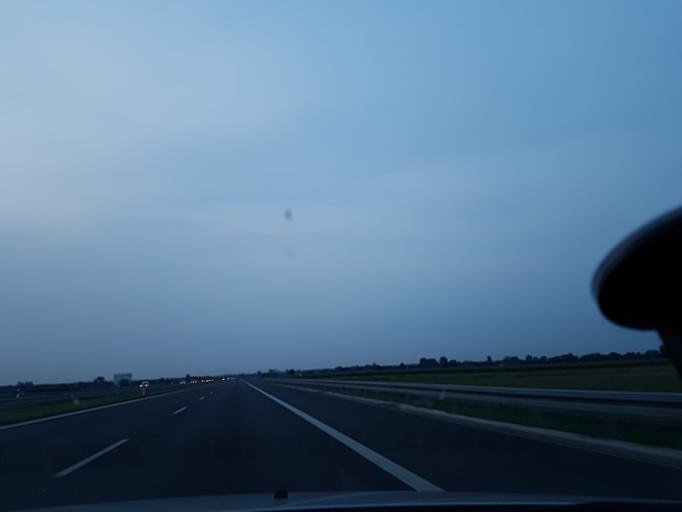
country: PL
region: Lodz Voivodeship
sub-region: Powiat zgierski
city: Strykow
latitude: 51.9724
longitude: 19.5734
